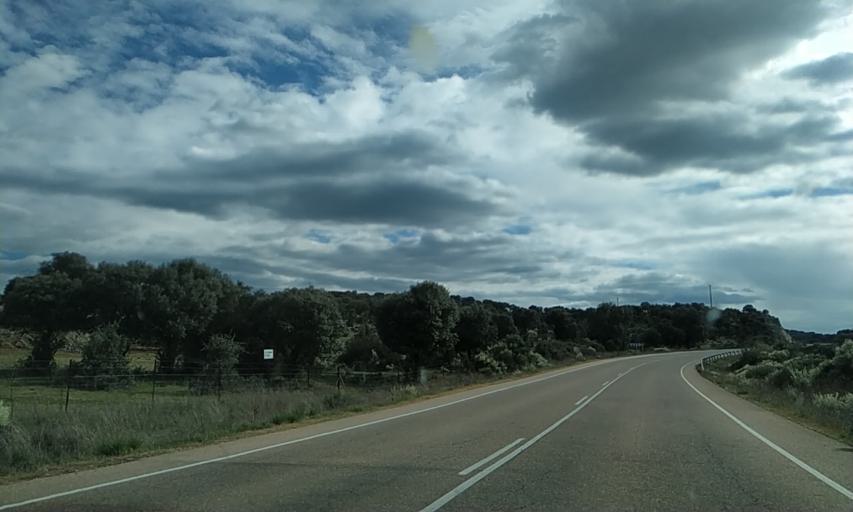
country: ES
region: Castille and Leon
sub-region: Provincia de Salamanca
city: Pastores
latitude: 40.5101
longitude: -6.5713
